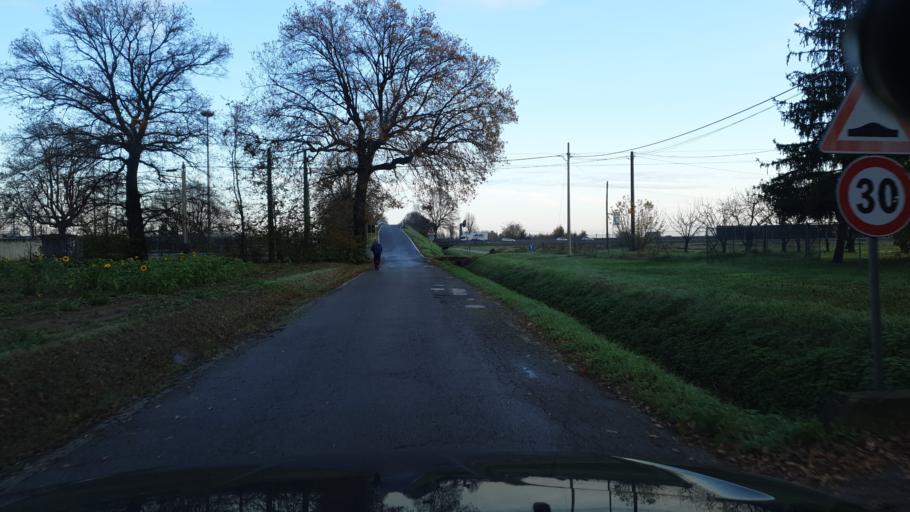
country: IT
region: Emilia-Romagna
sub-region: Provincia di Bologna
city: Crespellano
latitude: 44.5237
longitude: 11.1475
